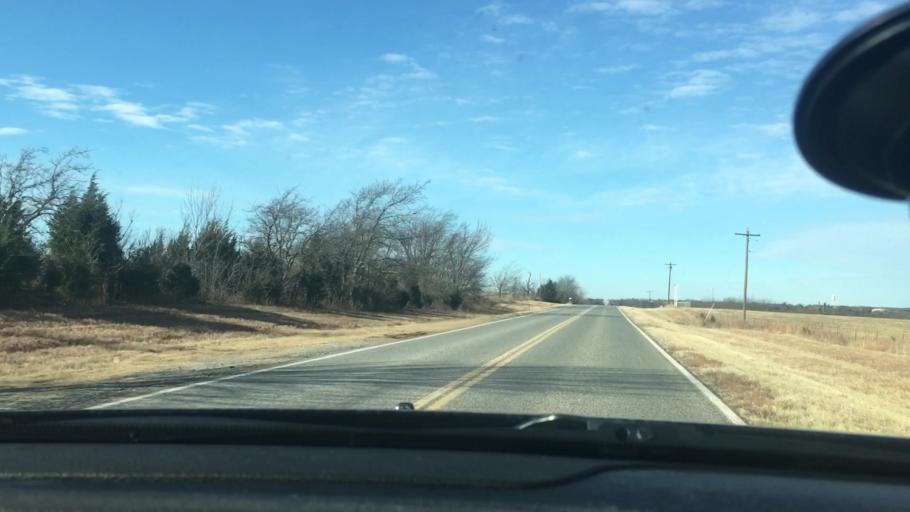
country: US
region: Oklahoma
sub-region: Seminole County
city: Konawa
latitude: 34.9859
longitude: -96.9030
